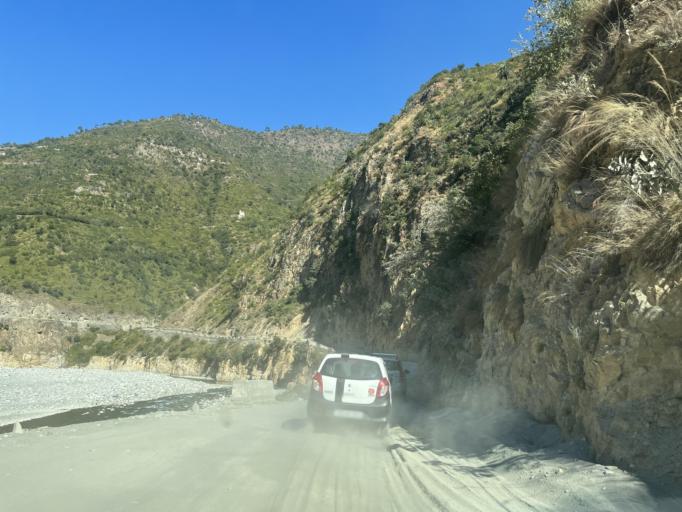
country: IN
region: Uttarakhand
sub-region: Naini Tal
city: Naini Tal
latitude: 29.5067
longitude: 79.4533
